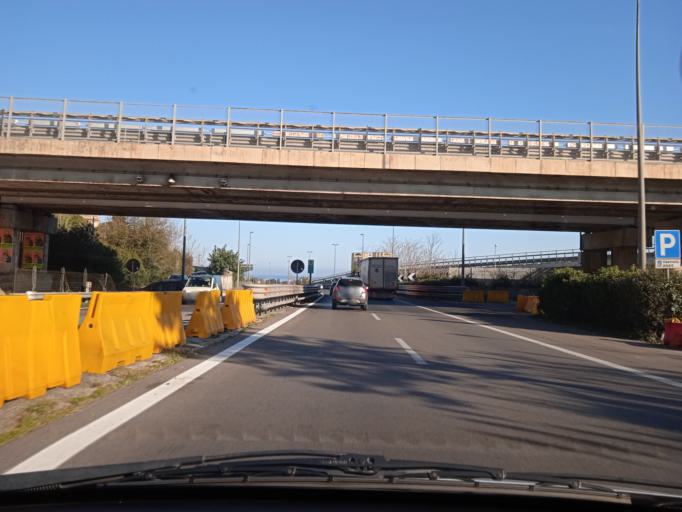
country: IT
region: Sicily
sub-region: Palermo
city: Isola delle Femmine
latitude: 38.1902
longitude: 13.2826
